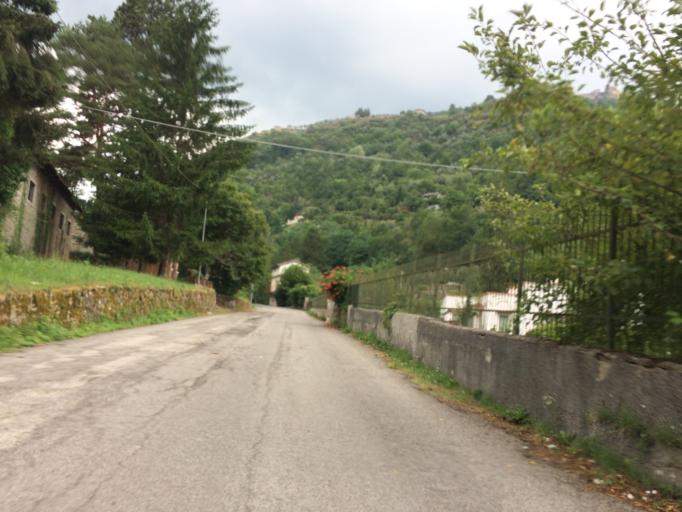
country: IT
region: Liguria
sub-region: Provincia di Imperia
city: Molini di Triora
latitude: 43.9865
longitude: 7.7753
